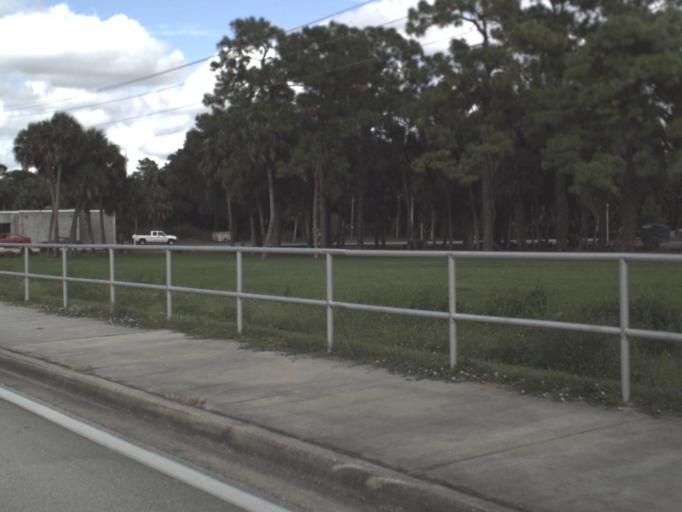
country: US
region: Florida
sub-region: Lee County
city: Palmona Park
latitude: 26.6849
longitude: -81.8844
